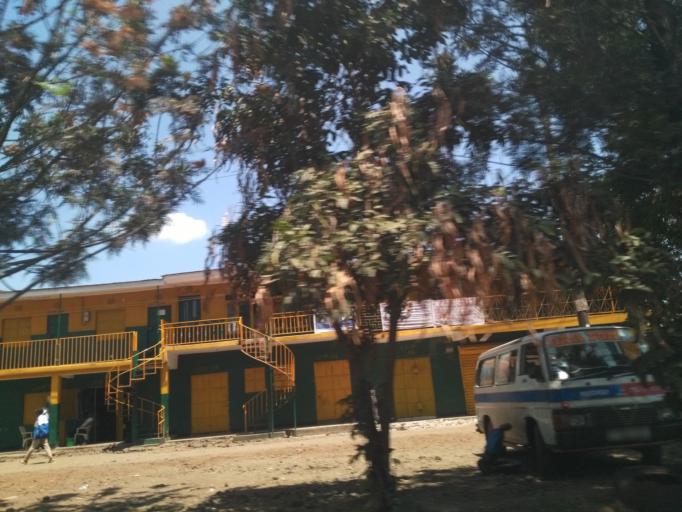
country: TZ
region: Arusha
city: Arusha
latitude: -3.3726
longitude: 36.6746
